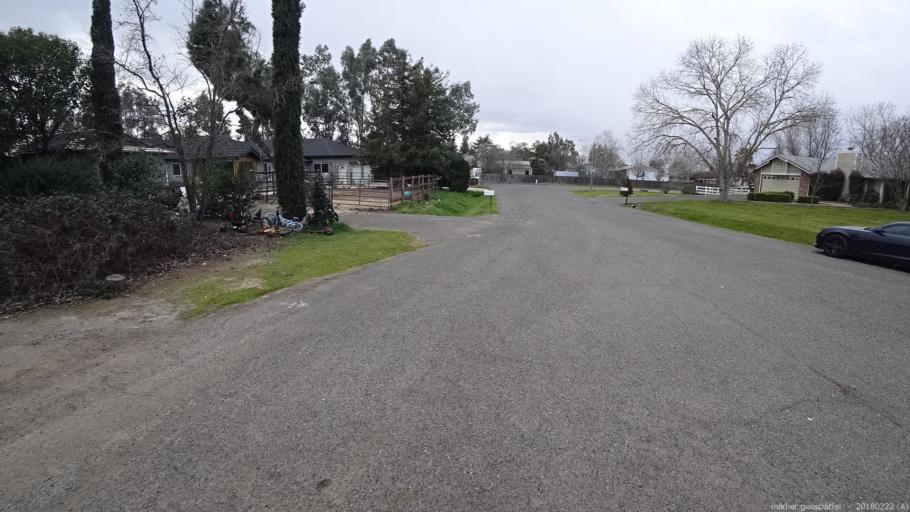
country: US
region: California
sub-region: Sacramento County
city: Rio Linda
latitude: 38.7057
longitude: -121.4175
